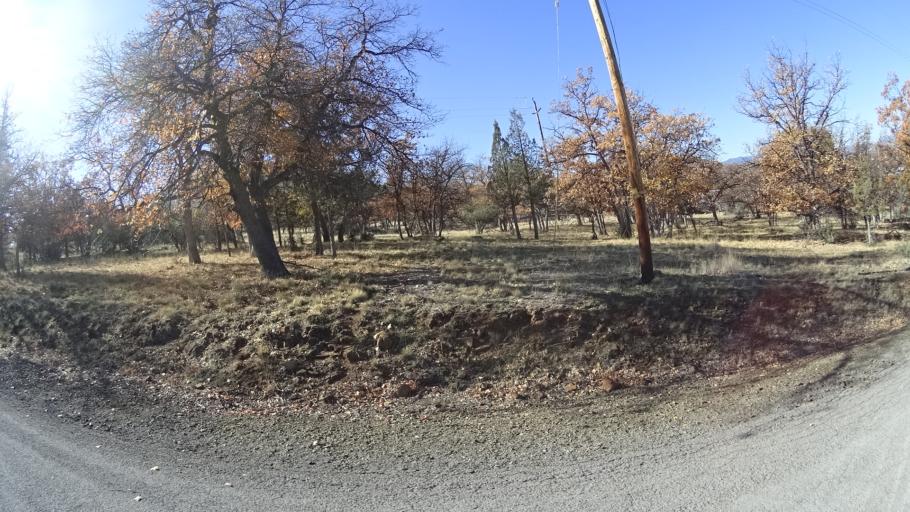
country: US
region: California
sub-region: Siskiyou County
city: Montague
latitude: 41.8821
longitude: -122.4875
